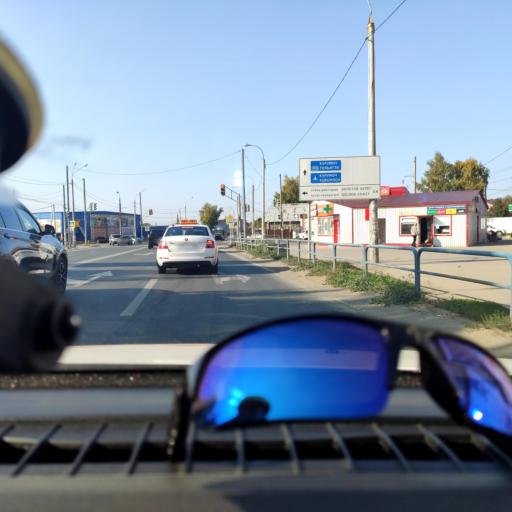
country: RU
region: Samara
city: Volzhskiy
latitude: 53.4258
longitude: 50.1223
